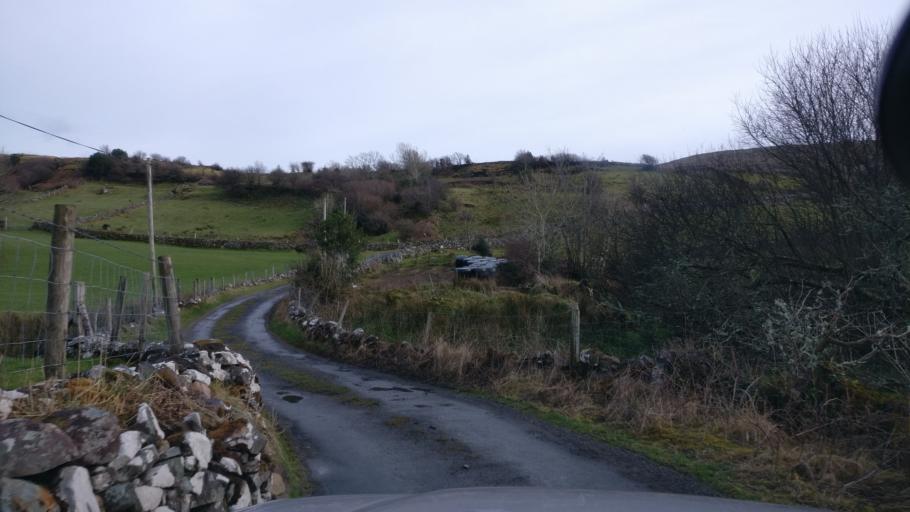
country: IE
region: Connaught
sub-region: County Galway
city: Oughterard
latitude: 53.5554
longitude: -9.4418
